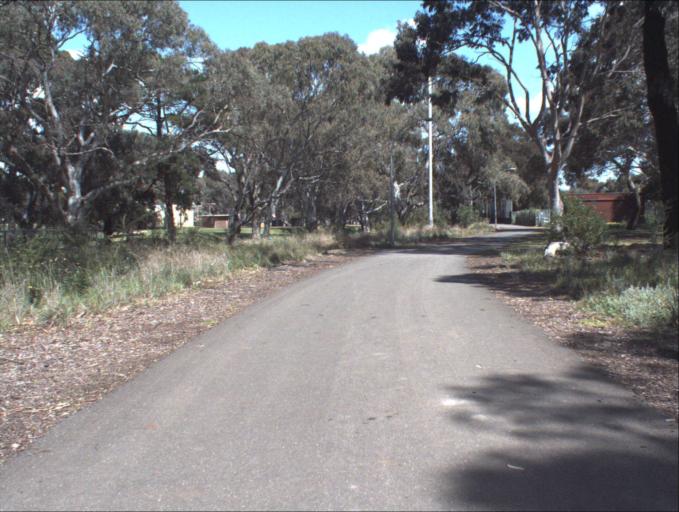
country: AU
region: South Australia
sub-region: Port Adelaide Enfield
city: Gilles Plains
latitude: -34.8433
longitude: 138.6664
